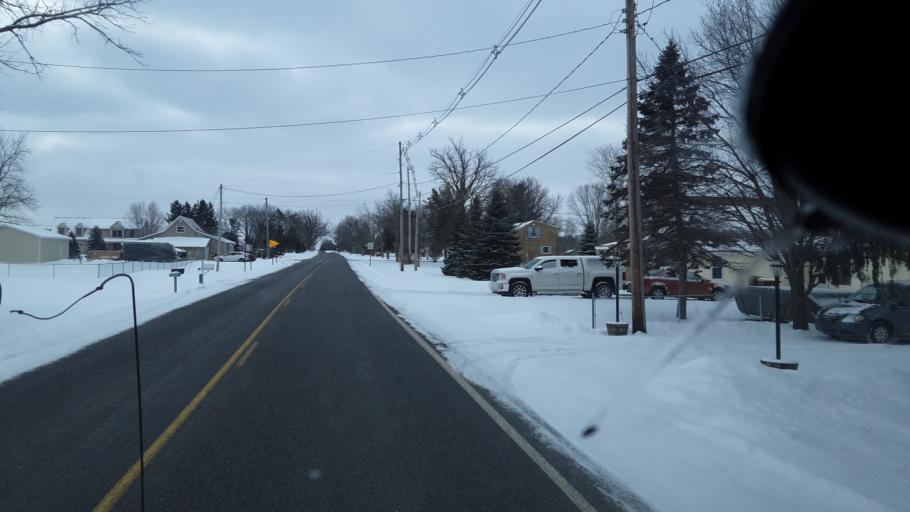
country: US
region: Michigan
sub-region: Ingham County
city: Holt
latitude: 42.5979
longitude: -84.5428
